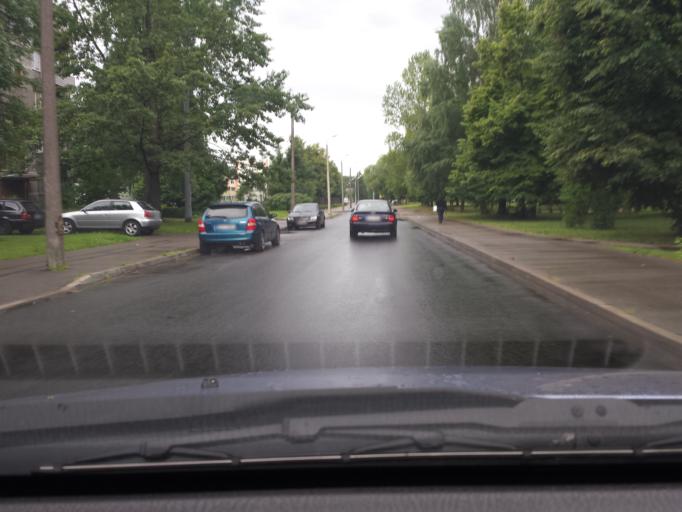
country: LV
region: Kekava
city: Kekava
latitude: 56.9037
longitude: 24.2093
